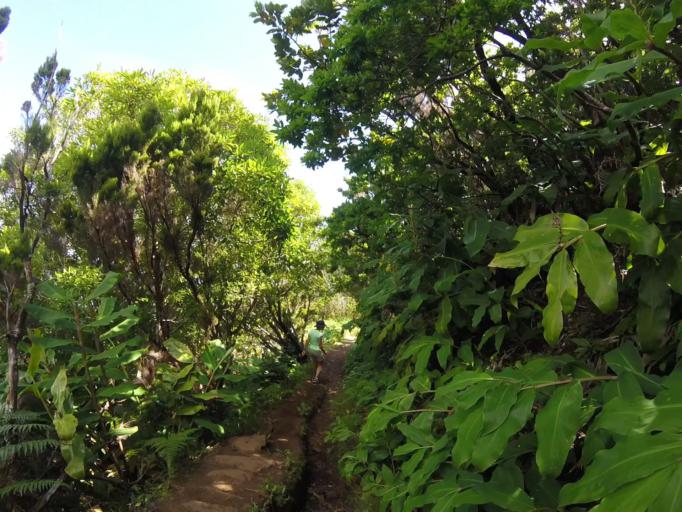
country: PT
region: Azores
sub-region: Sao Roque do Pico
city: Sao Roque do Pico
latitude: 38.6073
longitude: -27.9205
